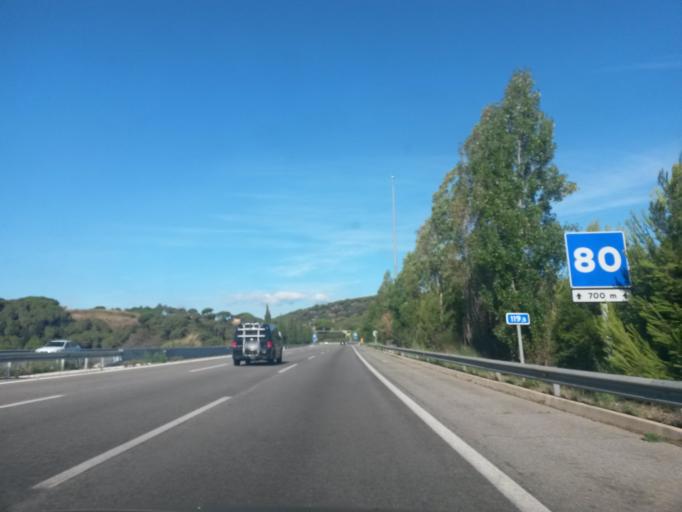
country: ES
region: Catalonia
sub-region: Provincia de Barcelona
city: Sant Pol de Mar
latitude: 41.6114
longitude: 2.6321
